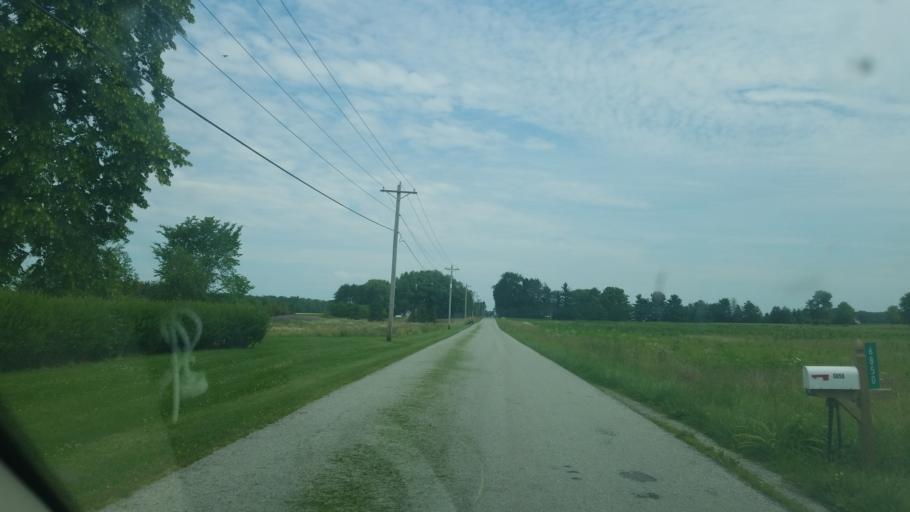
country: US
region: Ohio
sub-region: Seneca County
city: Fostoria
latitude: 41.0667
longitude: -83.4634
